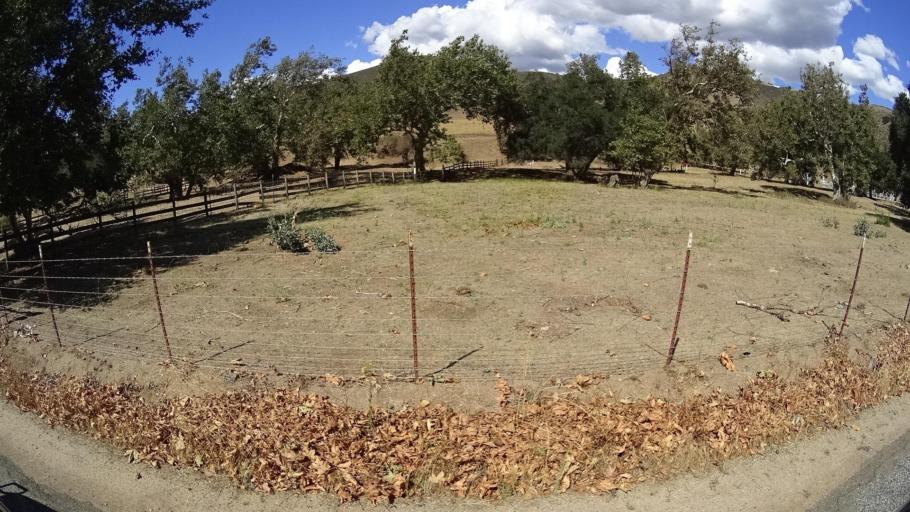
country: US
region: California
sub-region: Monterey County
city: Gonzales
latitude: 36.6029
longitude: -121.4161
